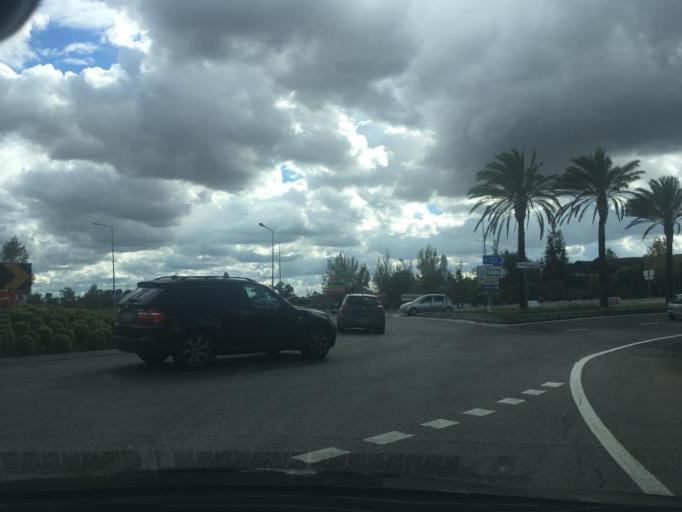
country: PT
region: Santarem
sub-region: Torres Novas
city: Torres Novas
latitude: 39.4645
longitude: -8.5299
